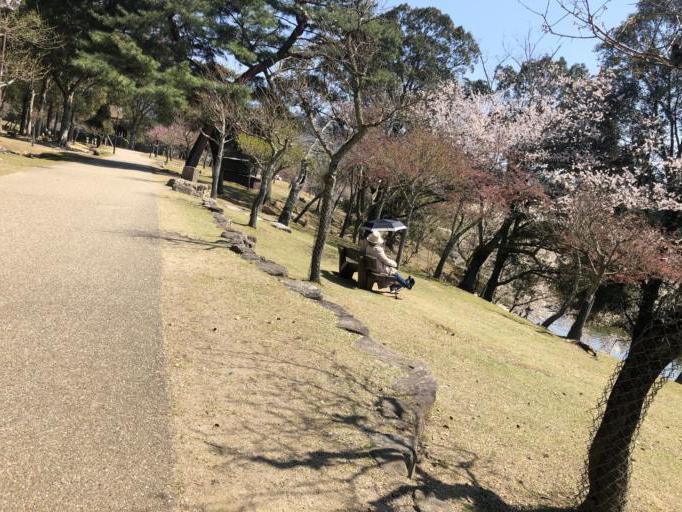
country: JP
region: Nara
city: Nara-shi
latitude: 34.6810
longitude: 135.8377
